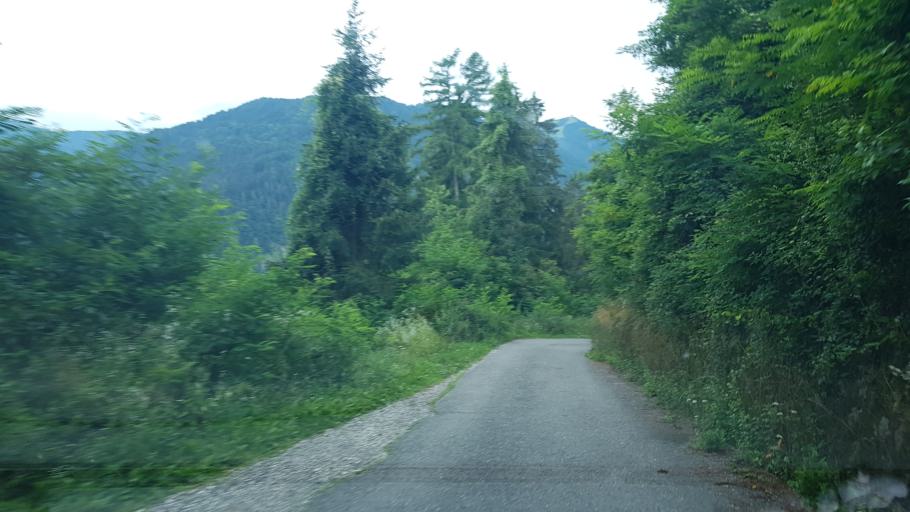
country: IT
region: Friuli Venezia Giulia
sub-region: Provincia di Udine
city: Cercivento
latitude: 46.5317
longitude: 12.9892
